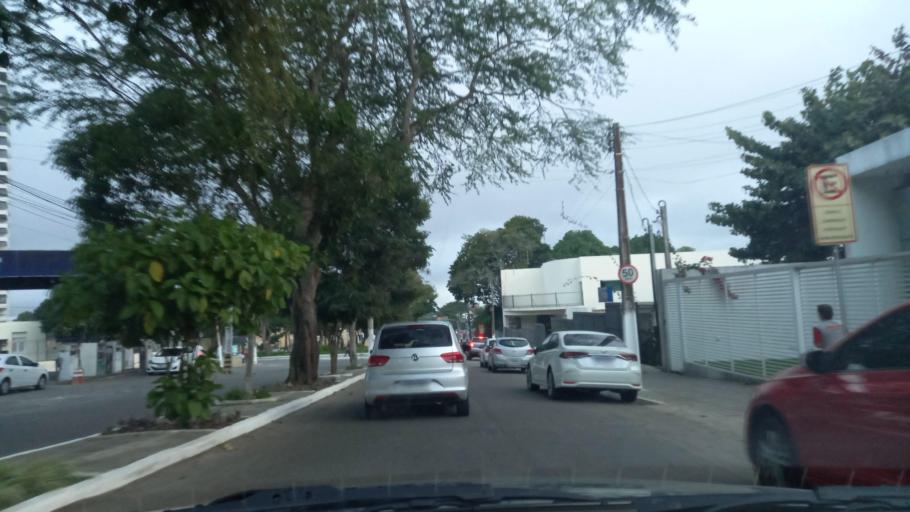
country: BR
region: Pernambuco
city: Garanhuns
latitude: -8.8802
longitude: -36.4766
